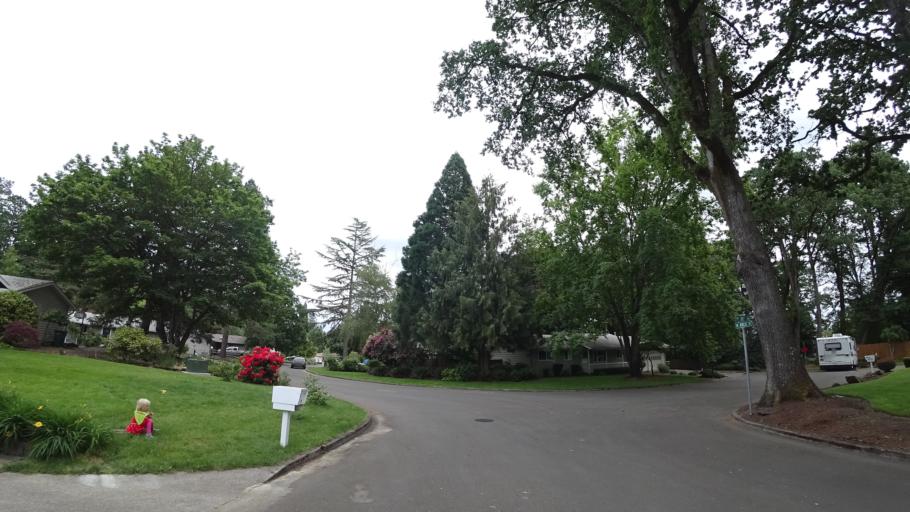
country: US
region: Oregon
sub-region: Washington County
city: Metzger
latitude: 45.4536
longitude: -122.7679
